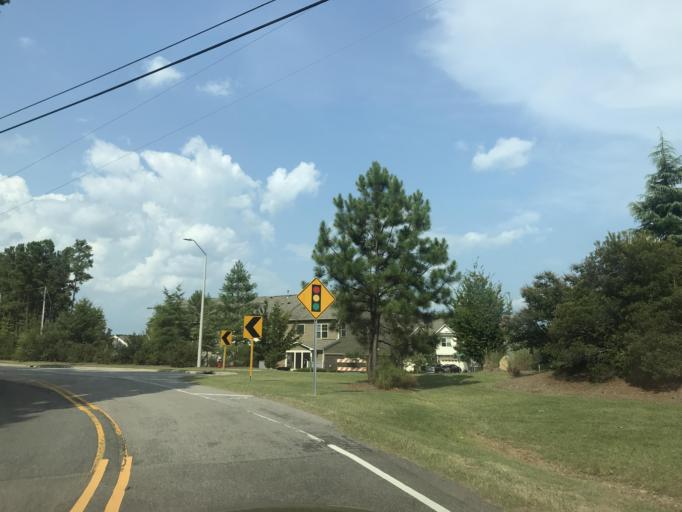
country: US
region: North Carolina
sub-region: Wake County
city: Morrisville
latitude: 35.8308
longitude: -78.8624
